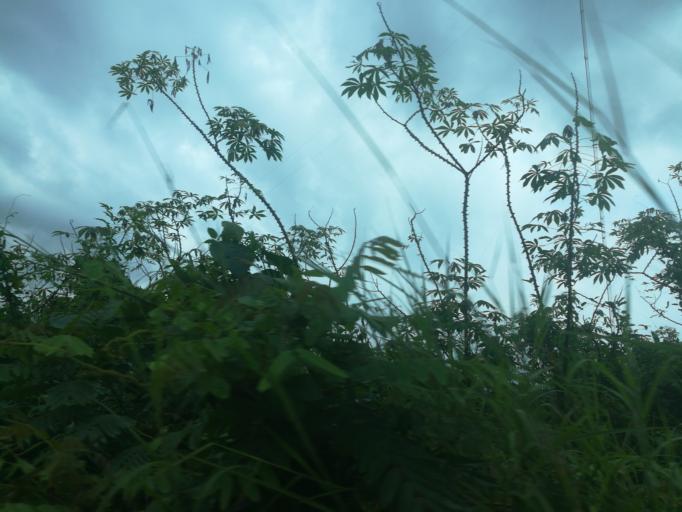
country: NG
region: Lagos
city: Ikorodu
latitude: 6.6641
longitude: 3.6168
